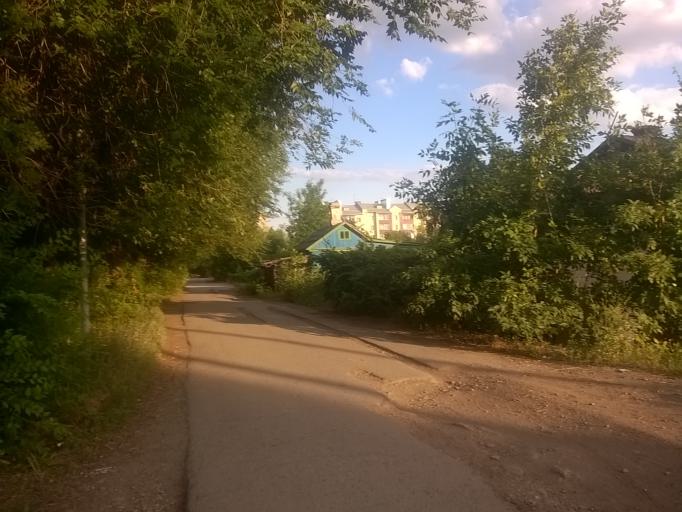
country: RU
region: Rostov
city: Donetsk
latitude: 48.3330
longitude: 39.9596
